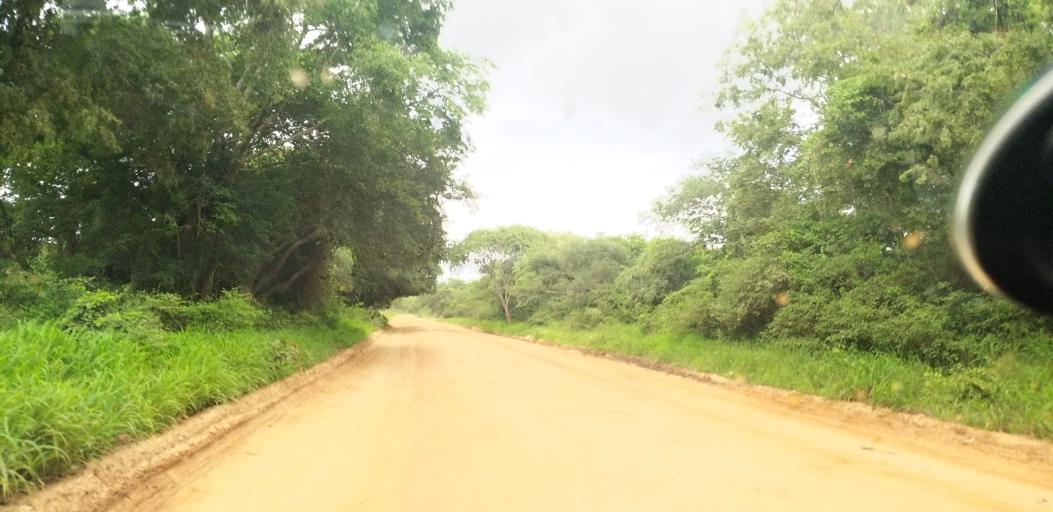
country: ZM
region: Lusaka
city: Lusaka
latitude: -15.1853
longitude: 28.4476
